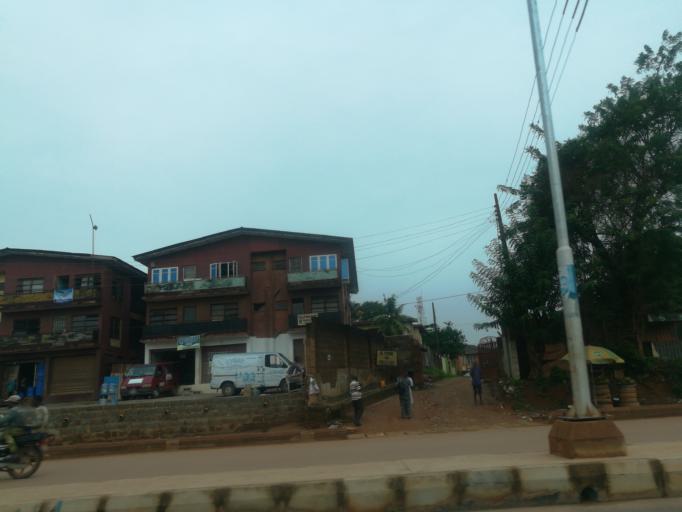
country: NG
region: Oyo
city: Ibadan
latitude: 7.3906
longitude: 3.9310
